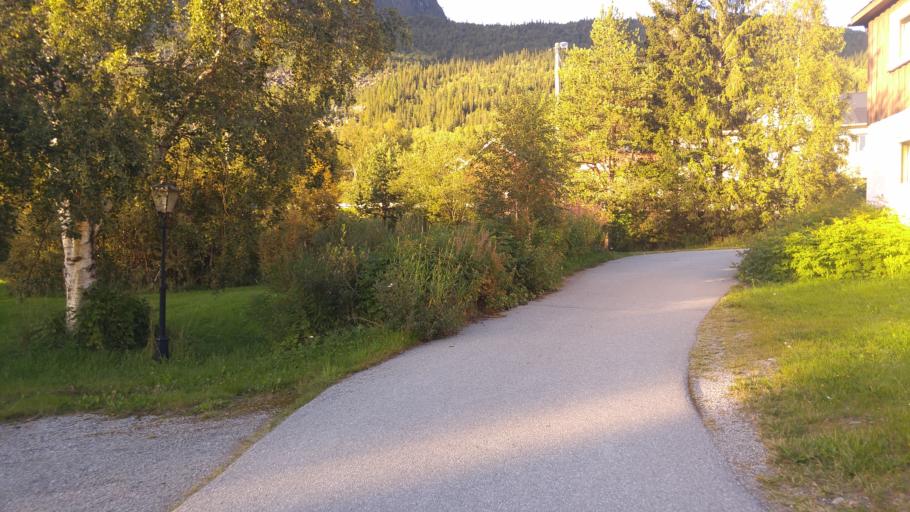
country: NO
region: Buskerud
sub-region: Hemsedal
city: Troim
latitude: 60.8509
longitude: 8.6143
